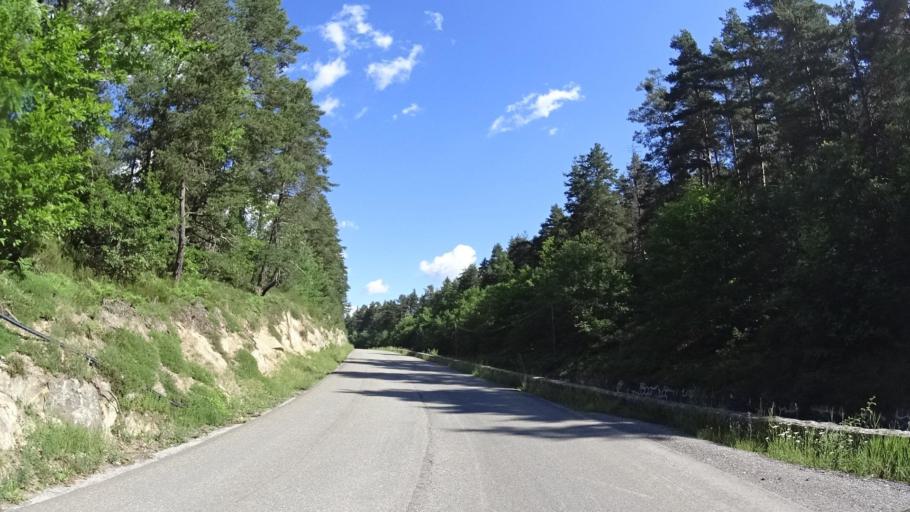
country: FR
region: Provence-Alpes-Cote d'Azur
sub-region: Departement des Alpes-de-Haute-Provence
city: Annot
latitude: 43.9819
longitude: 6.6501
